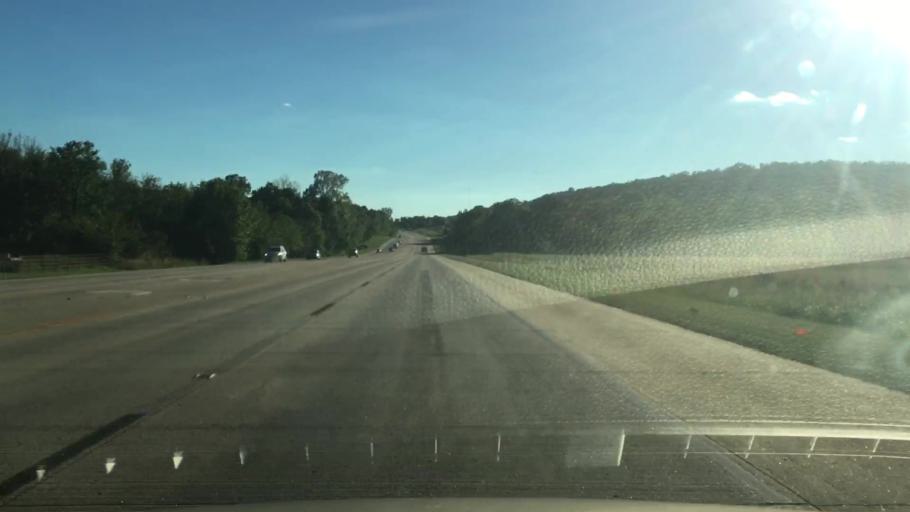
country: US
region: Oklahoma
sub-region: Cherokee County
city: Park Hill
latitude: 35.8411
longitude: -95.0334
